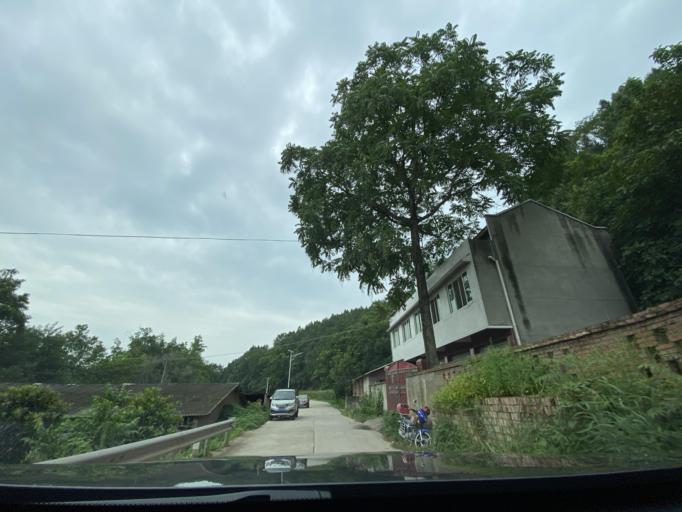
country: CN
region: Sichuan
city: Jiancheng
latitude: 30.3883
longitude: 104.5110
